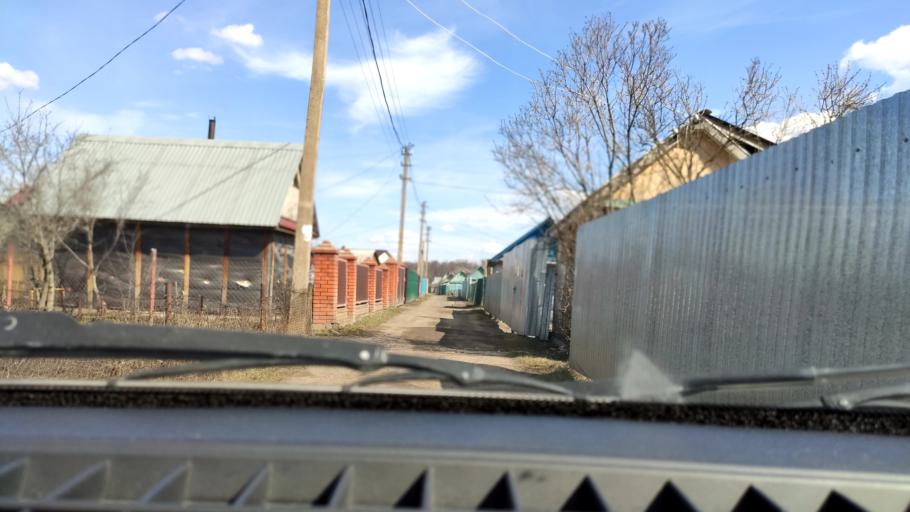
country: RU
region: Bashkortostan
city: Avdon
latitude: 54.6772
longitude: 55.8180
